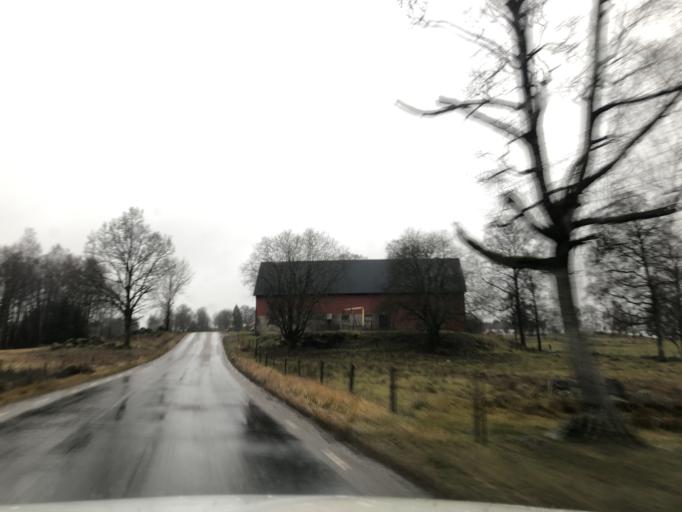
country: SE
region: Vaestra Goetaland
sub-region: Ulricehamns Kommun
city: Ulricehamn
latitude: 57.8519
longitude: 13.5460
